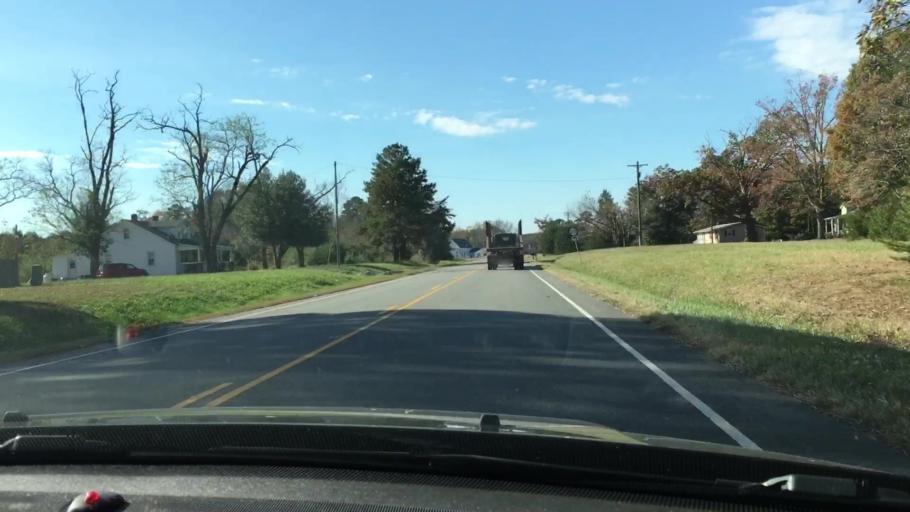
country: US
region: Virginia
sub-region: King William County
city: Central Garage
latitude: 37.7915
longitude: -77.2069
